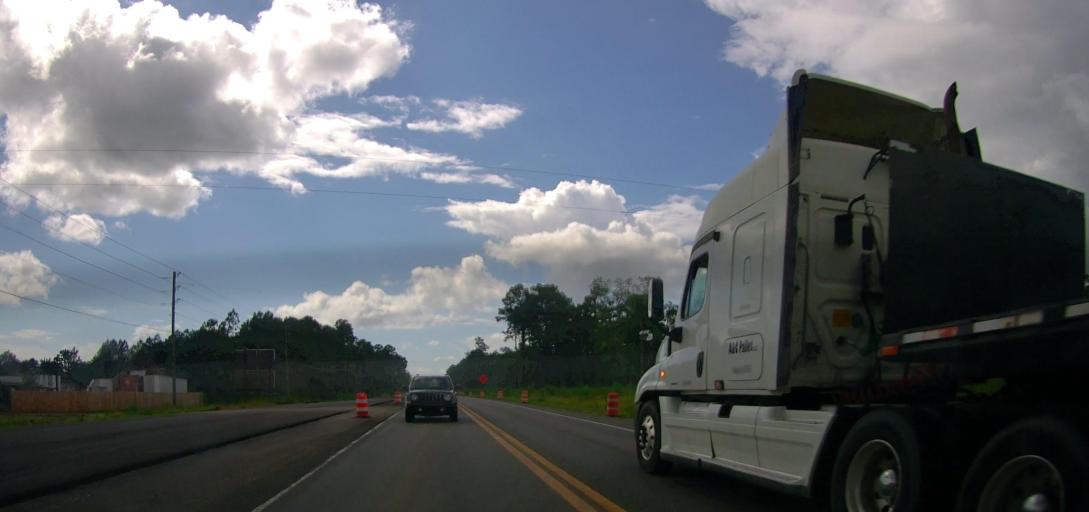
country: US
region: Georgia
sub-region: Coffee County
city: Douglas
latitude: 31.5236
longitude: -82.8981
